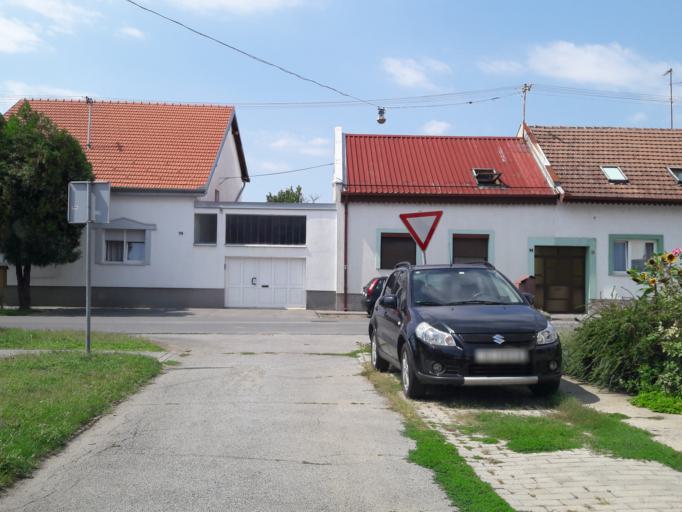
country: HR
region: Osjecko-Baranjska
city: Visnjevac
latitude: 45.5602
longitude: 18.6480
